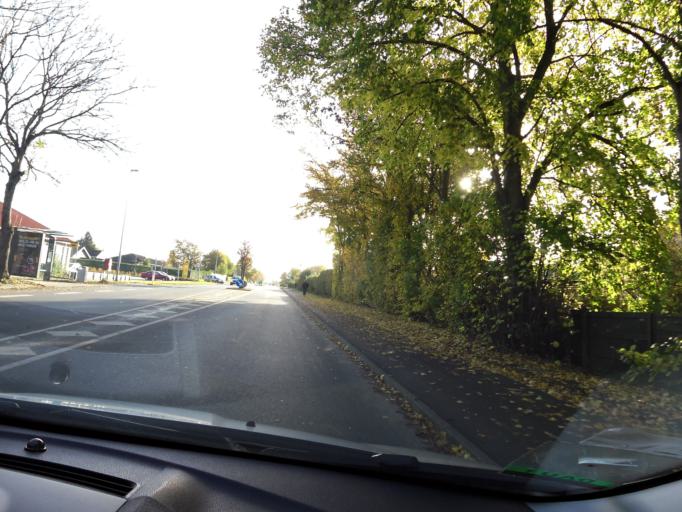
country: DK
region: South Denmark
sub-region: Odense Kommune
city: Hojby
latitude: 55.3418
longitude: 10.4280
